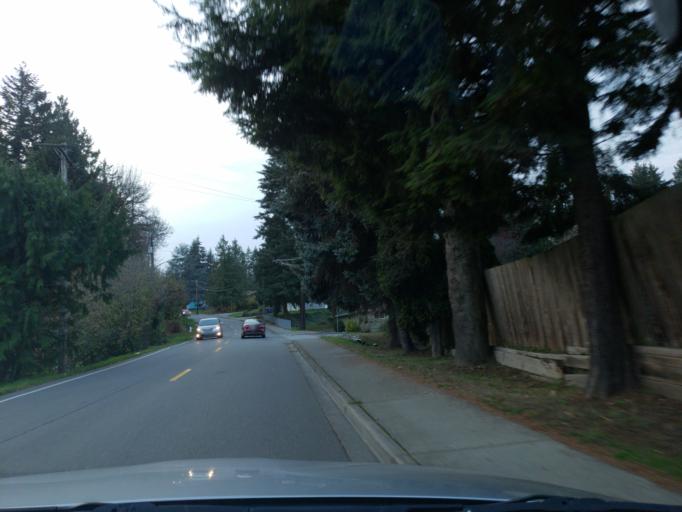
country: US
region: Washington
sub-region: King County
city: Bothell
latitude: 47.7666
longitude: -122.2137
